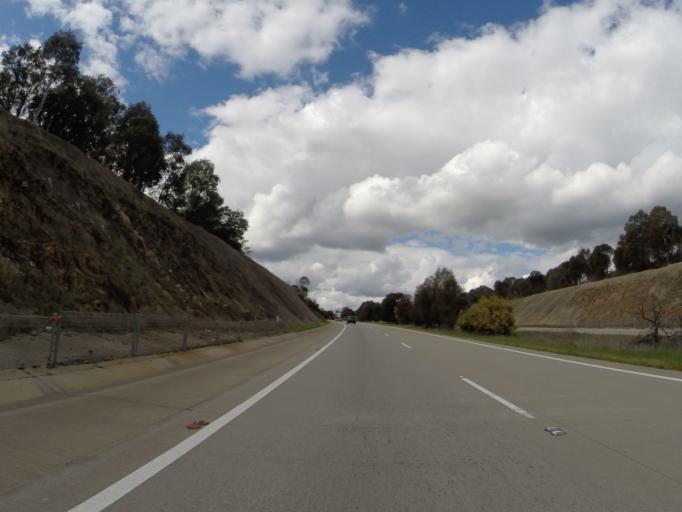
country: AU
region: New South Wales
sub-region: Yass Valley
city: Murrumbateman
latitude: -34.8010
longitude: 149.1537
